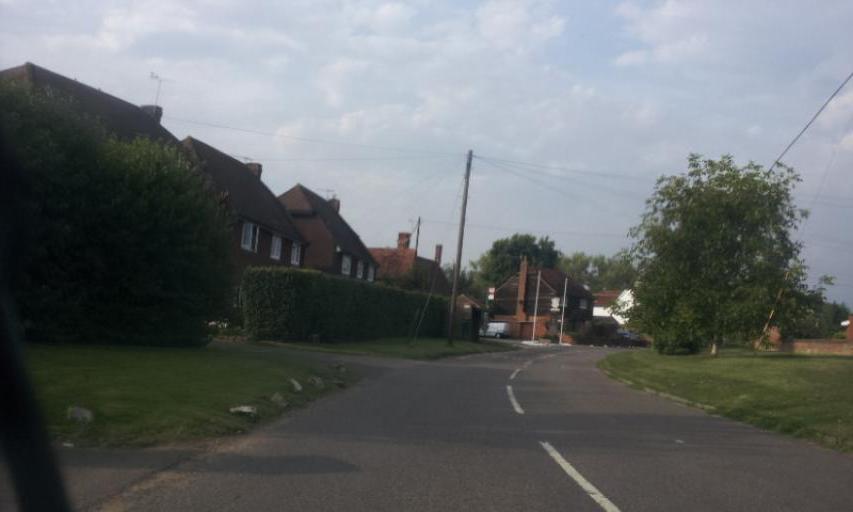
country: GB
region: England
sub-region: Kent
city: Yalding
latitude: 51.2068
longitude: 0.4179
